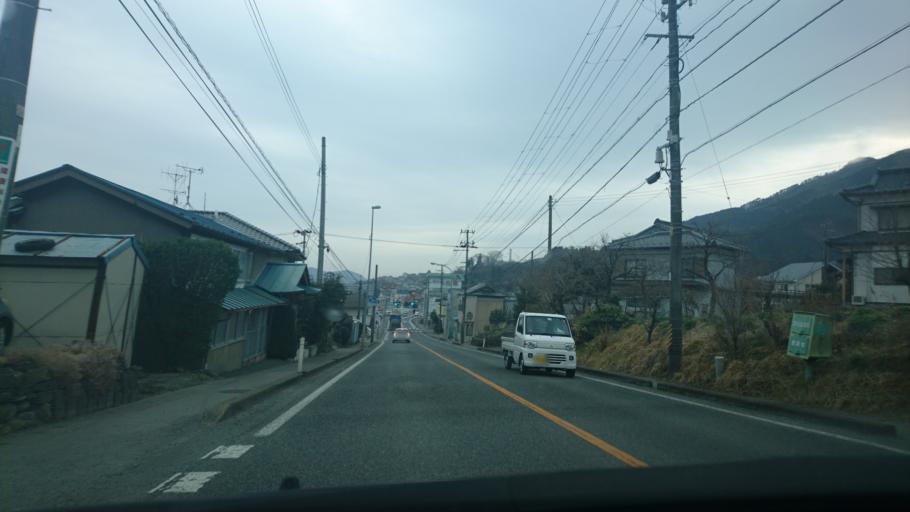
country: JP
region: Iwate
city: Ofunato
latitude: 39.0644
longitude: 141.7180
